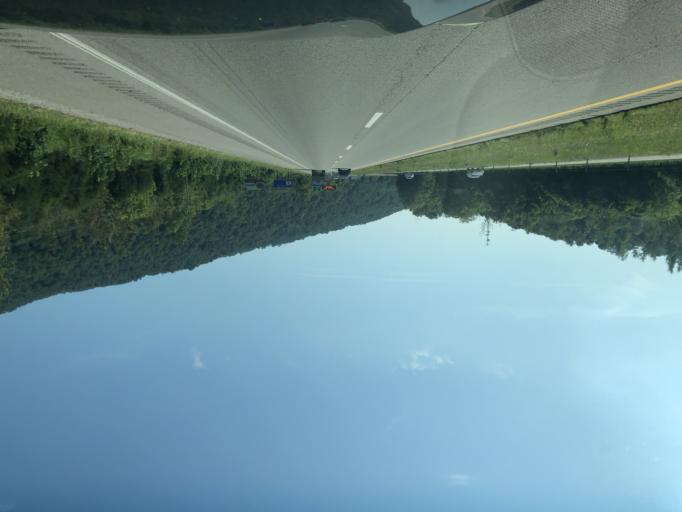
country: US
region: Tennessee
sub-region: Marion County
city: Monteagle
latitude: 35.1612
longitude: -85.7888
